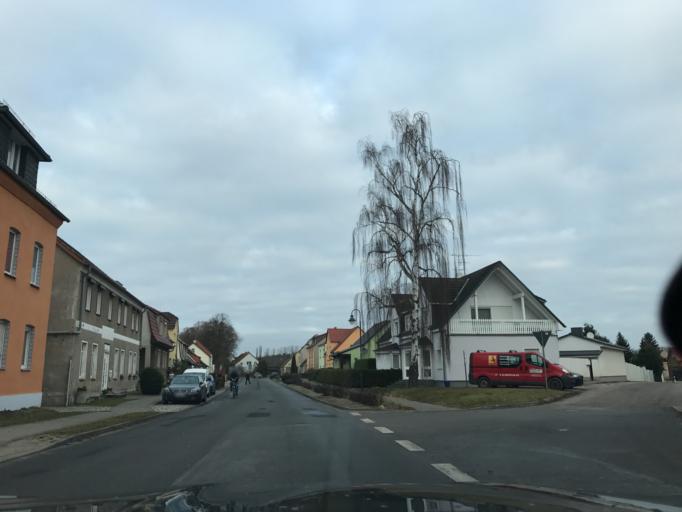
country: DE
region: Brandenburg
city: Gross Kreutz
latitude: 52.3205
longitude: 12.7362
